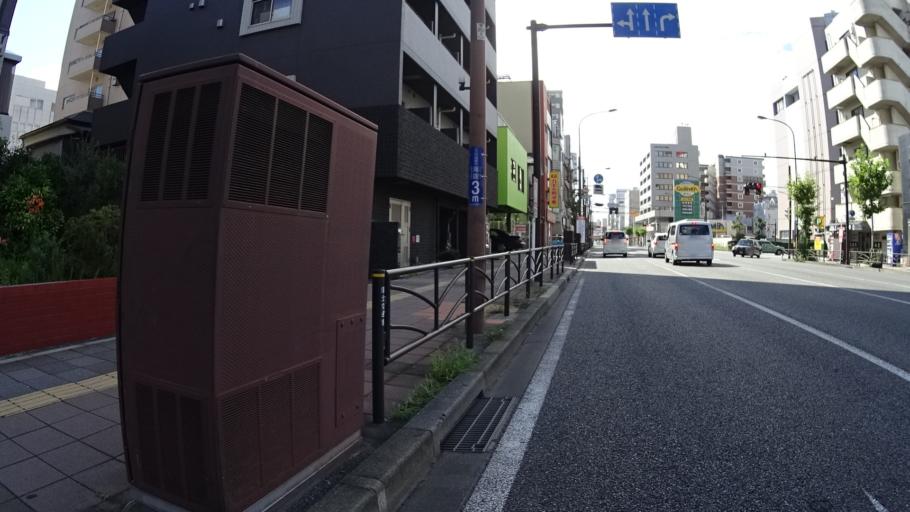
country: JP
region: Kanagawa
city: Yokosuka
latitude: 35.2800
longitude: 139.6734
